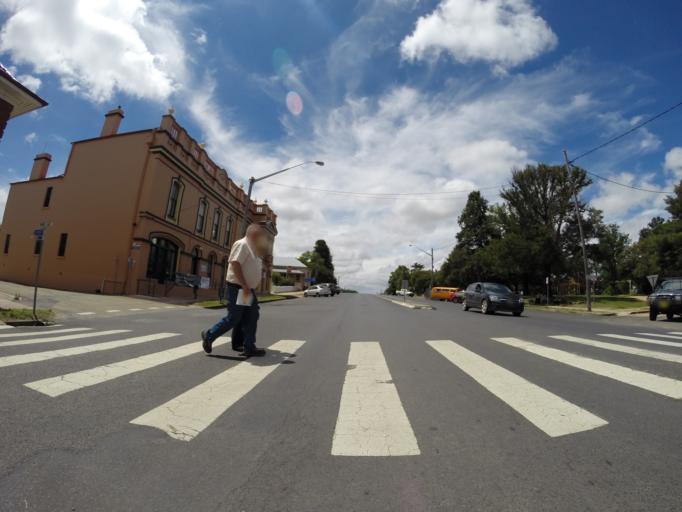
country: AU
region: New South Wales
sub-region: Palerang
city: Braidwood
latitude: -35.4433
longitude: 149.7996
